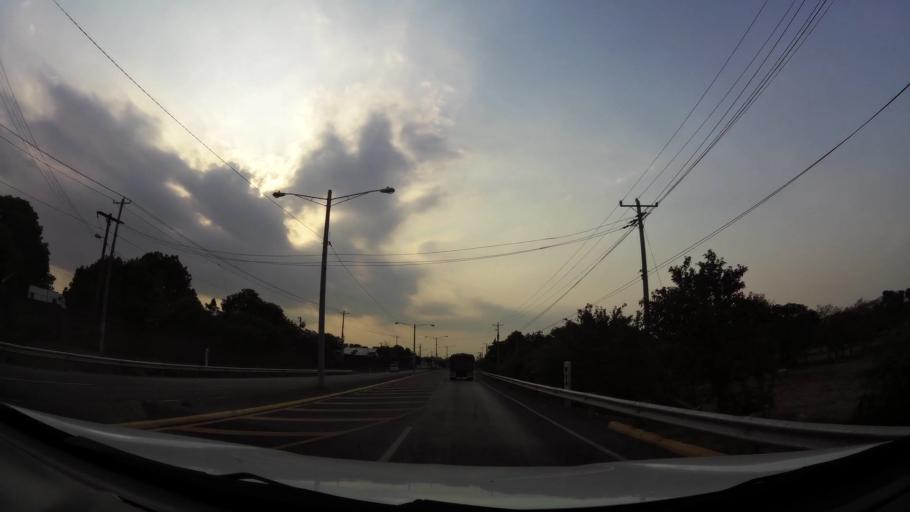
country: NI
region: Managua
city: Ciudad Sandino
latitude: 12.1780
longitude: -86.3524
